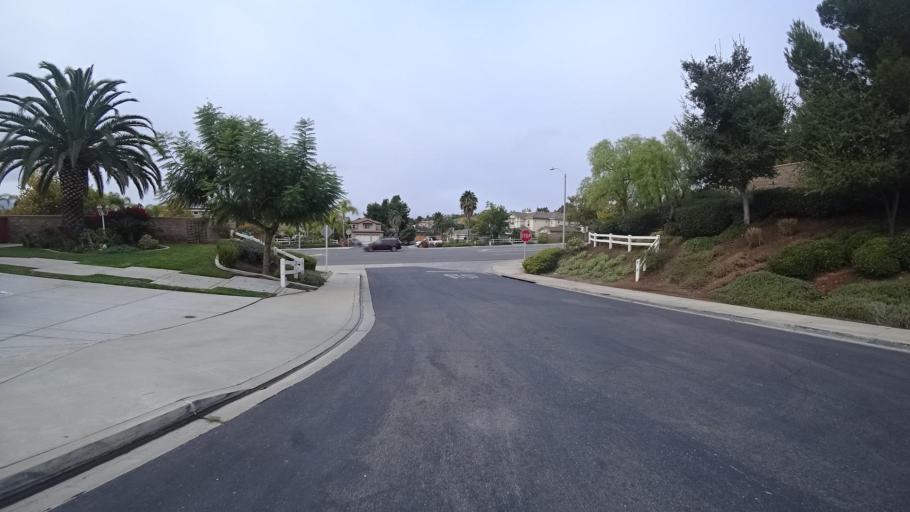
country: US
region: California
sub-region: San Diego County
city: Rancho San Diego
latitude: 32.7643
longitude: -116.9221
